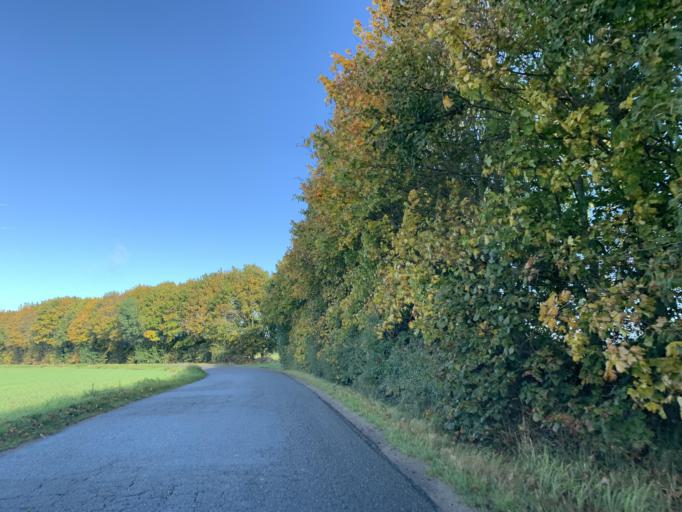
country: DE
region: Mecklenburg-Vorpommern
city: Gross Nemerow
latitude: 53.4719
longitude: 13.2691
